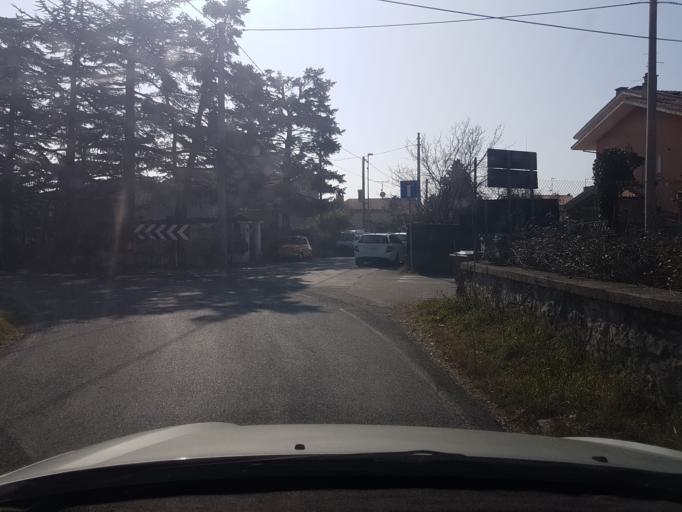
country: IT
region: Friuli Venezia Giulia
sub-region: Provincia di Trieste
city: Sistiana-Visogliano
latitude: 45.7753
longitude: 13.6401
